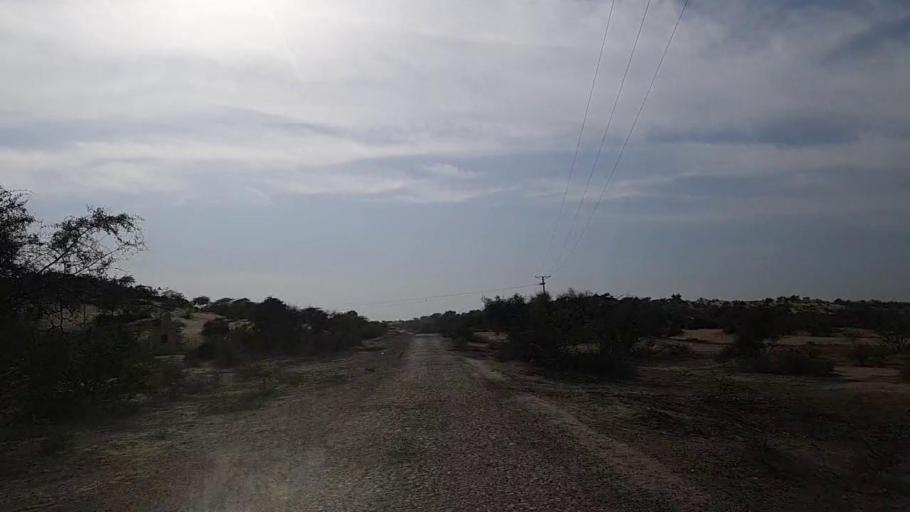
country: PK
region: Sindh
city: Umarkot
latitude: 25.1718
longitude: 69.9691
